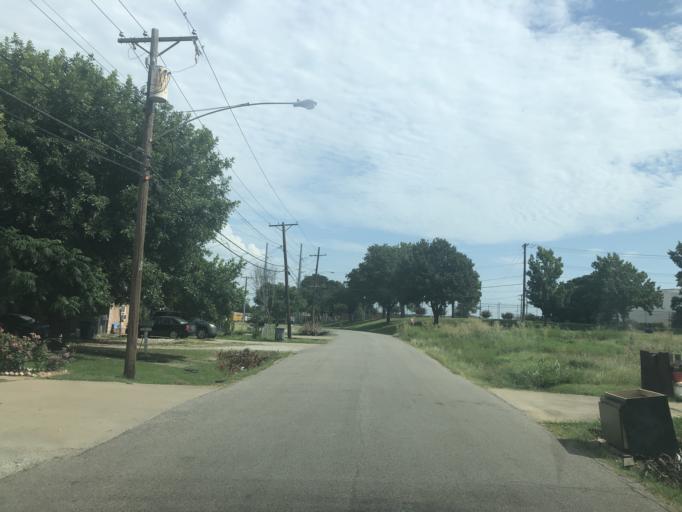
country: US
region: Texas
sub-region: Dallas County
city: Dallas
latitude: 32.8160
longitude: -96.8557
